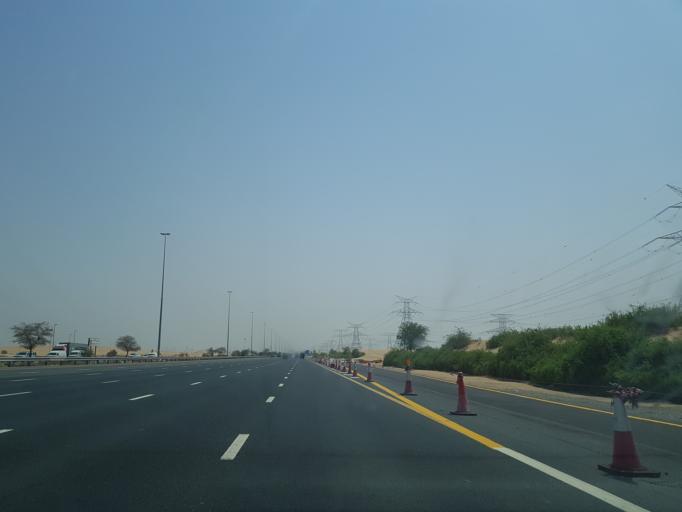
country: AE
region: Ash Shariqah
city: Sharjah
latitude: 25.1120
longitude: 55.4286
